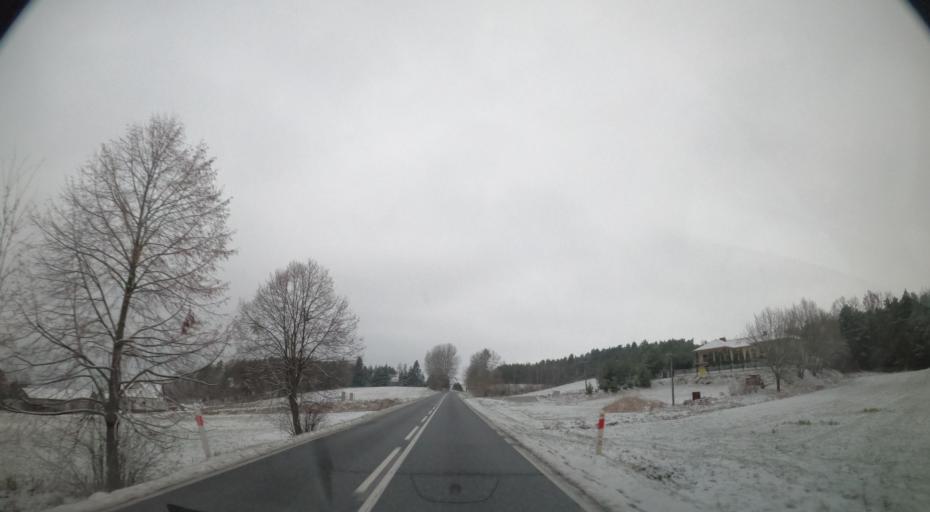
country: PL
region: Masovian Voivodeship
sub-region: Powiat plocki
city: Nowy Duninow
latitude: 52.5874
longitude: 19.5167
